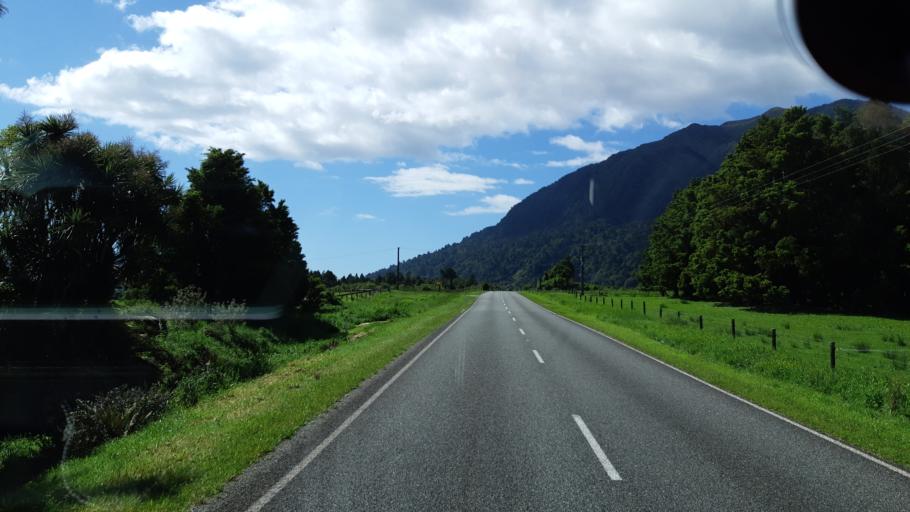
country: NZ
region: West Coast
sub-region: Westland District
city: Hokitika
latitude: -43.1183
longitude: 170.6334
